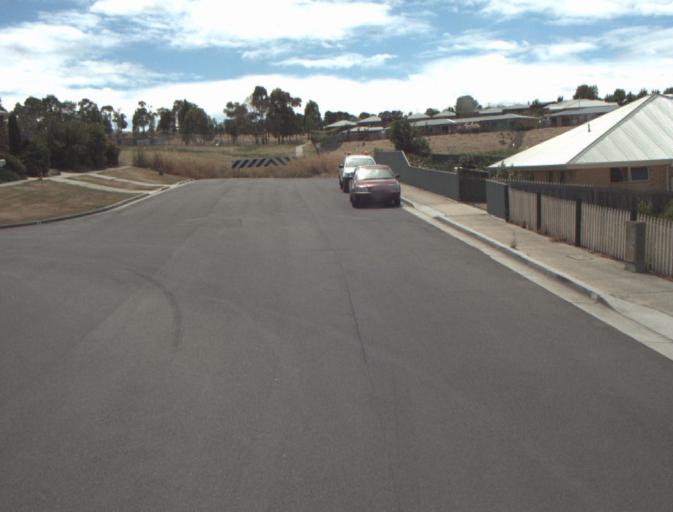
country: AU
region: Tasmania
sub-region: Launceston
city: Mayfield
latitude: -41.3812
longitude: 147.1212
